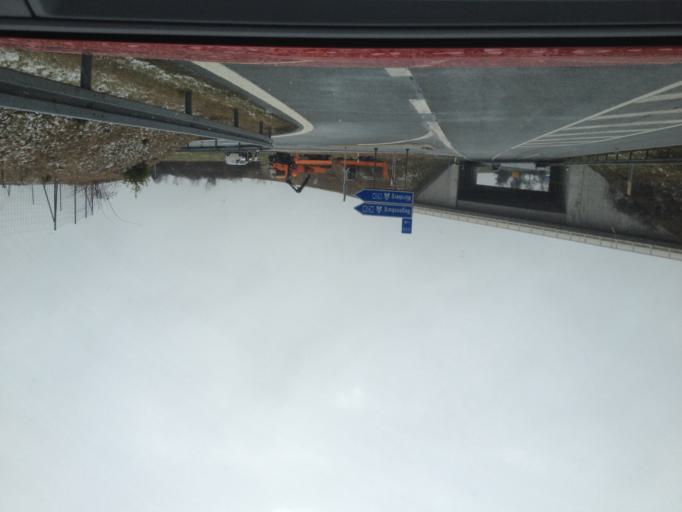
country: DE
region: Bavaria
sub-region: Upper Franconia
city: Gattendorf
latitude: 50.3117
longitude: 12.0218
